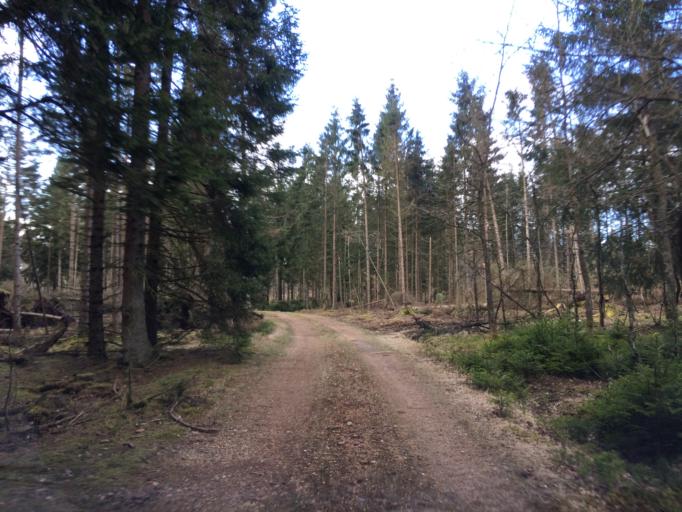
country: DK
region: Central Jutland
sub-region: Holstebro Kommune
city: Ulfborg
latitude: 56.2739
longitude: 8.4465
